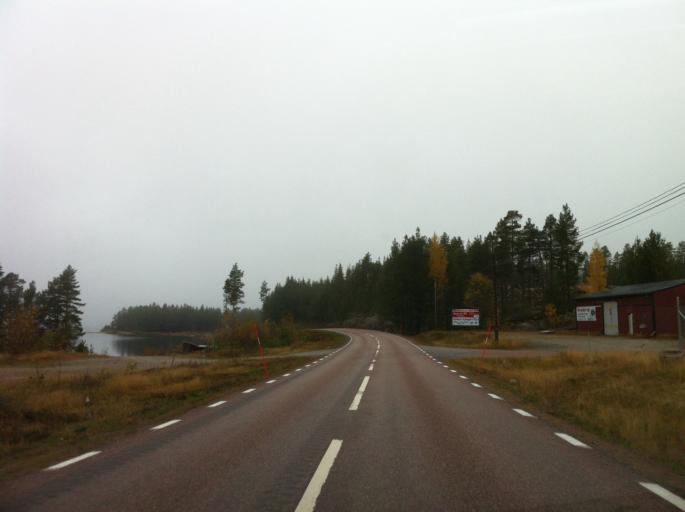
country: NO
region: Hedmark
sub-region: Trysil
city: Innbygda
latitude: 61.8504
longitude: 12.7598
